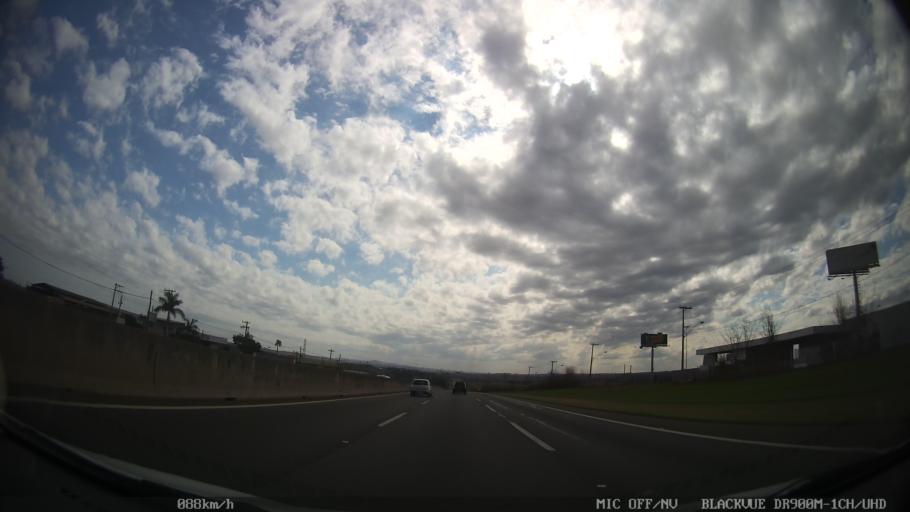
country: BR
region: Sao Paulo
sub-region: Limeira
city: Limeira
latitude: -22.6275
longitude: -47.3402
